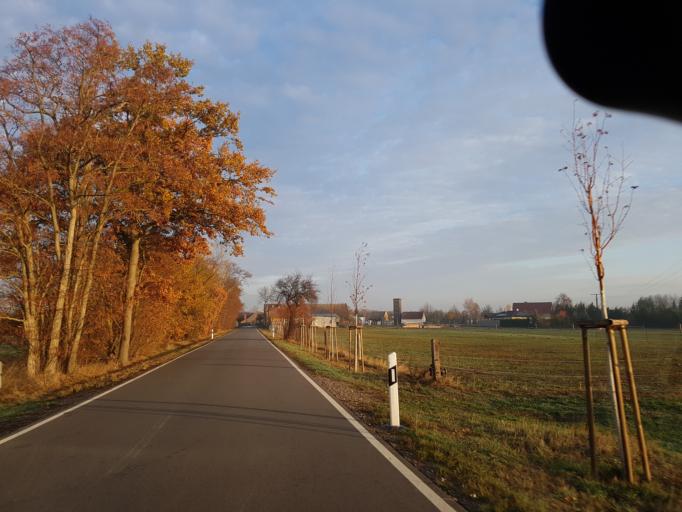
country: DE
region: Saxony-Anhalt
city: Elster
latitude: 51.8626
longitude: 12.8452
